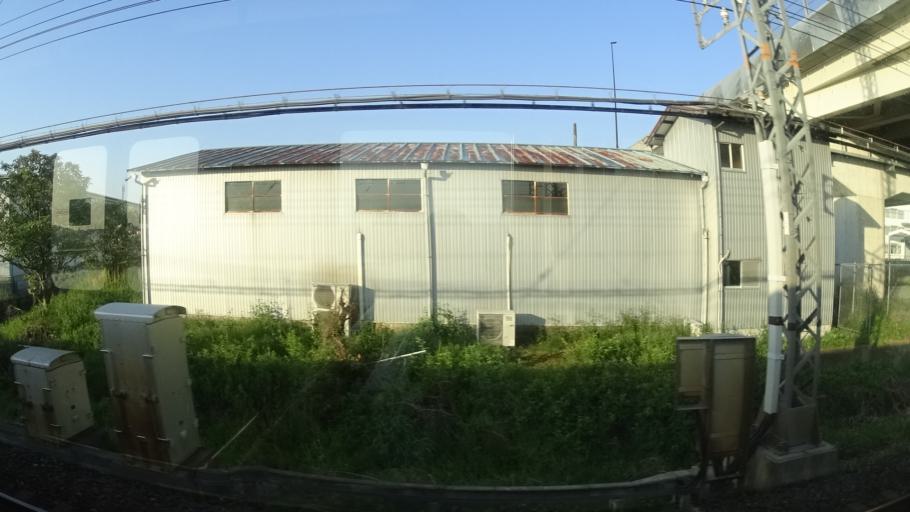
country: JP
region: Mie
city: Hisai-motomachi
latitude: 34.5578
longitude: 136.5624
